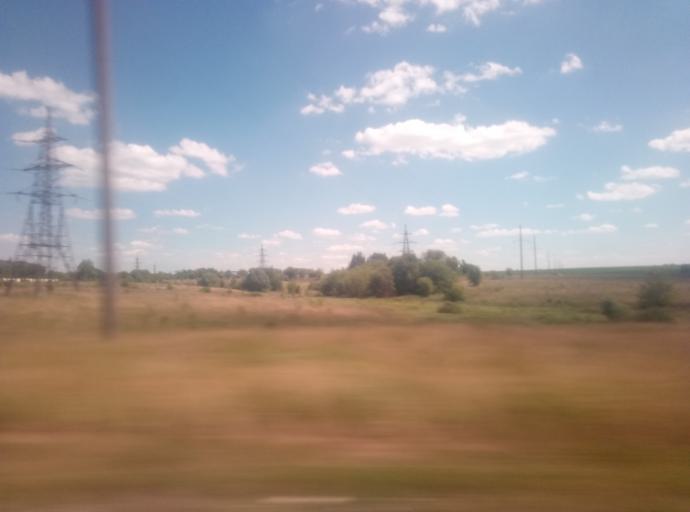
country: RU
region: Tula
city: Kireyevsk
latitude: 53.9516
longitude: 37.9391
